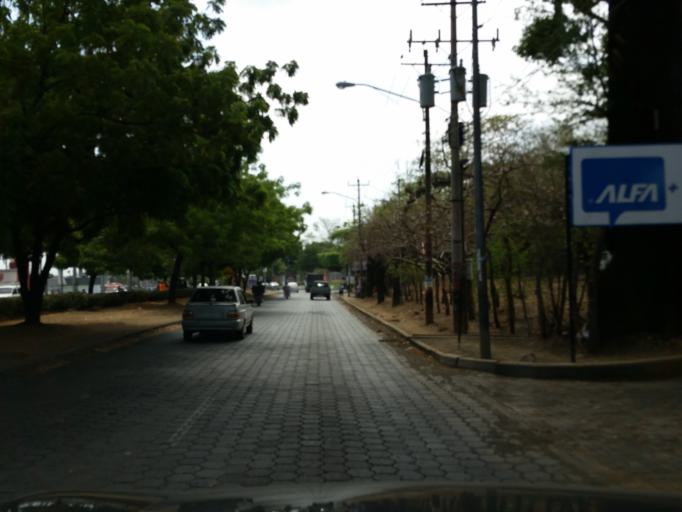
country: NI
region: Managua
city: Managua
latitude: 12.1126
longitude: -86.2577
